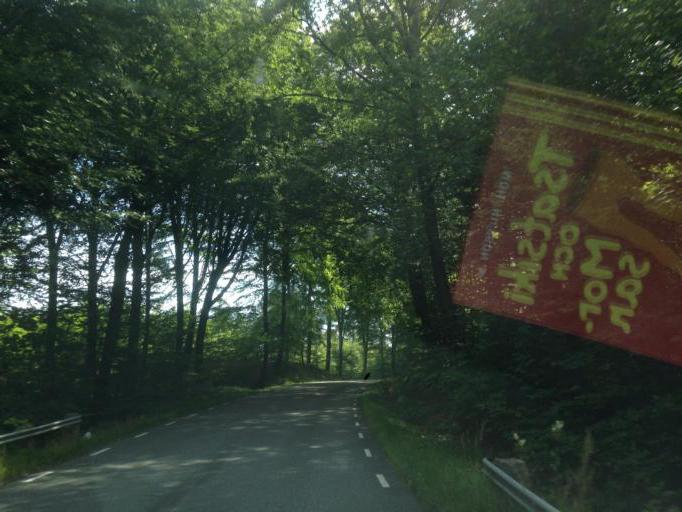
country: SE
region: Skane
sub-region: Tomelilla Kommun
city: Tomelilla
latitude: 55.6439
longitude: 14.0481
